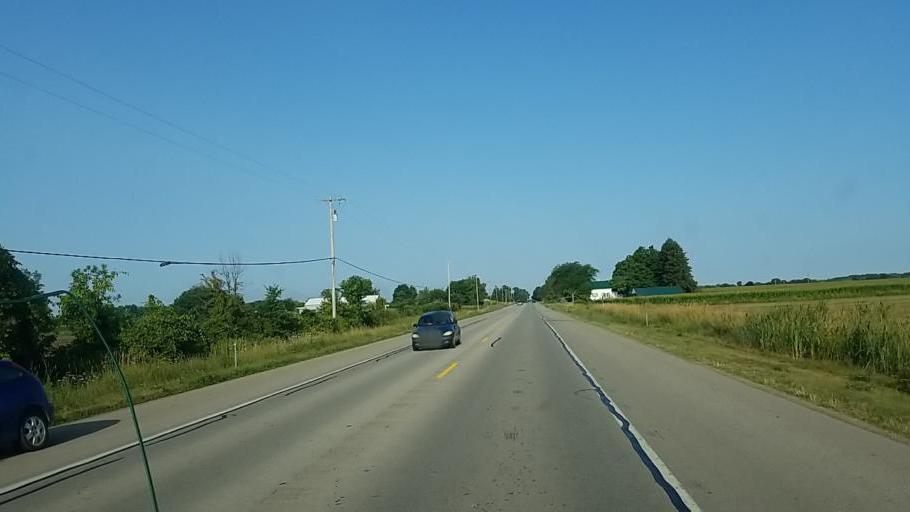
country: US
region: Michigan
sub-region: Newaygo County
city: Fremont
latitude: 43.4673
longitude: -86.0101
